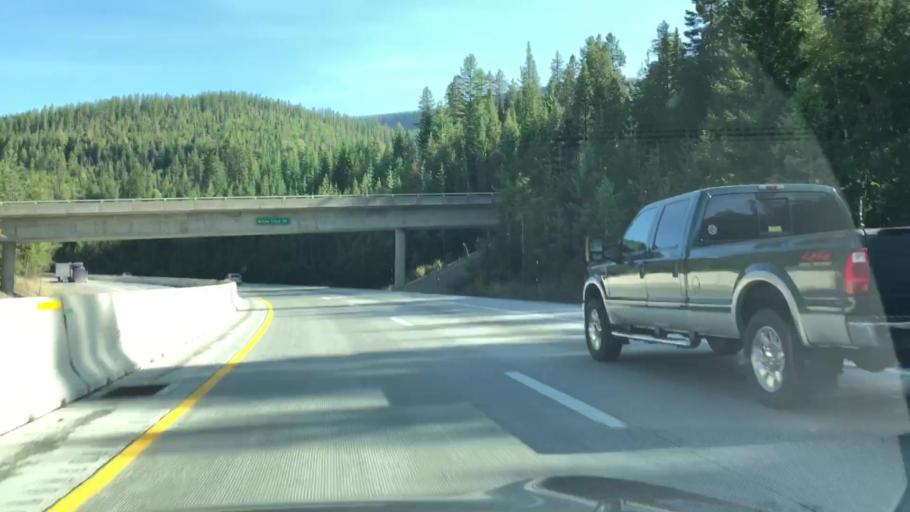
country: US
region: Idaho
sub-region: Shoshone County
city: Wallace
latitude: 47.4669
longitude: -115.7592
